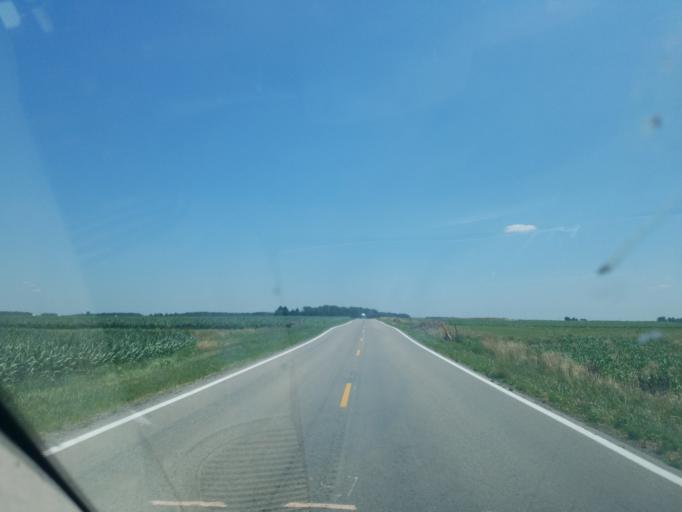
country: US
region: Ohio
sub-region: Allen County
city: Spencerville
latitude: 40.7426
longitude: -84.4642
